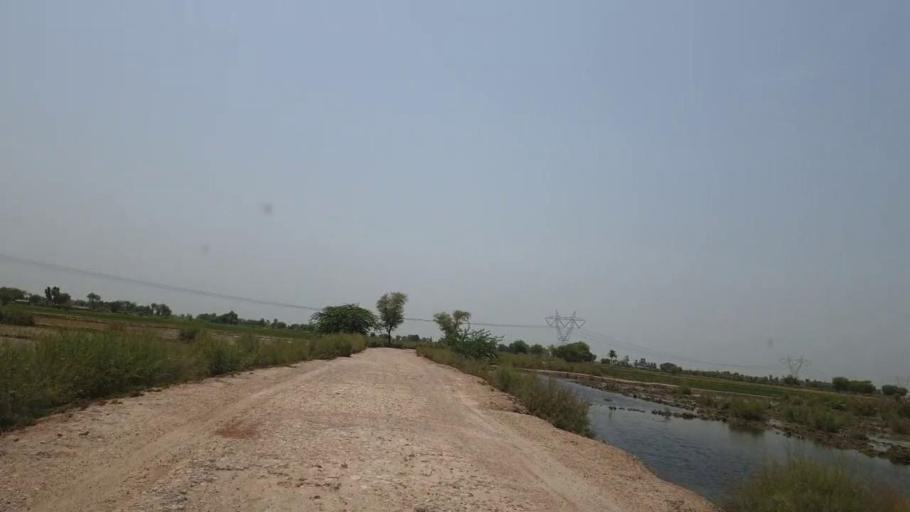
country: PK
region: Sindh
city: Shikarpur
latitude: 27.8920
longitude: 68.6309
